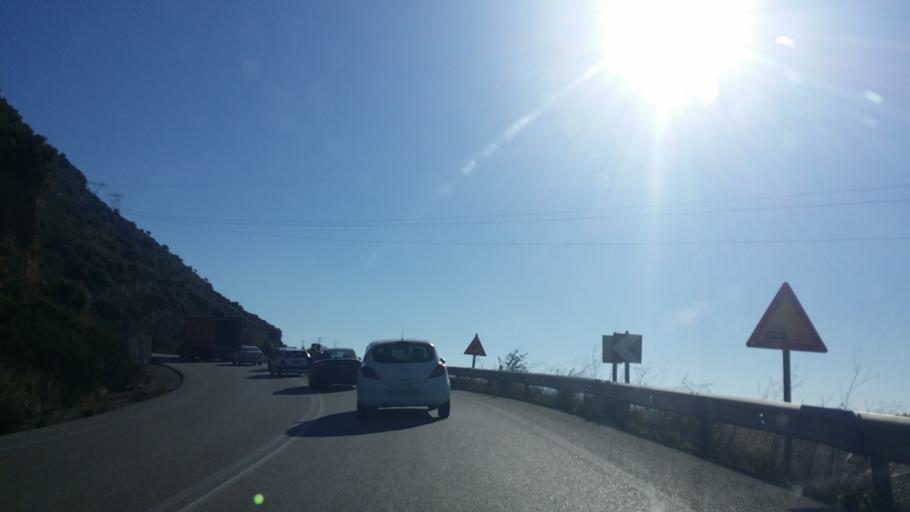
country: GR
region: West Greece
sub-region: Nomos Aitolias kai Akarnanias
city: Galatas
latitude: 38.3567
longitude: 21.6647
